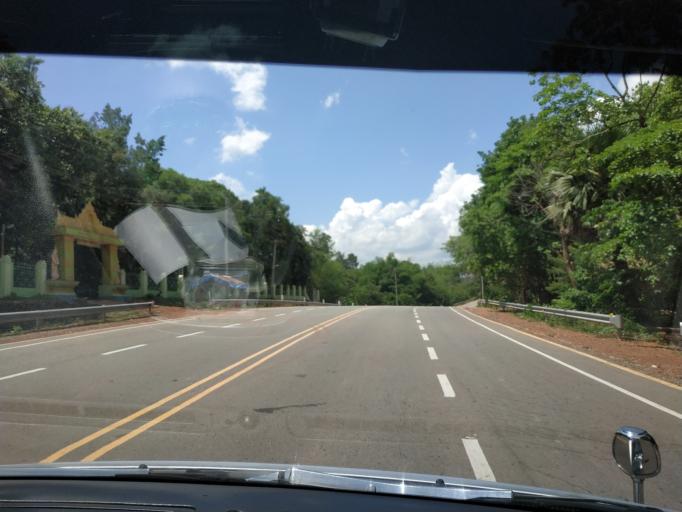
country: MM
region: Mon
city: Kyaikto
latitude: 17.3511
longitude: 97.0387
